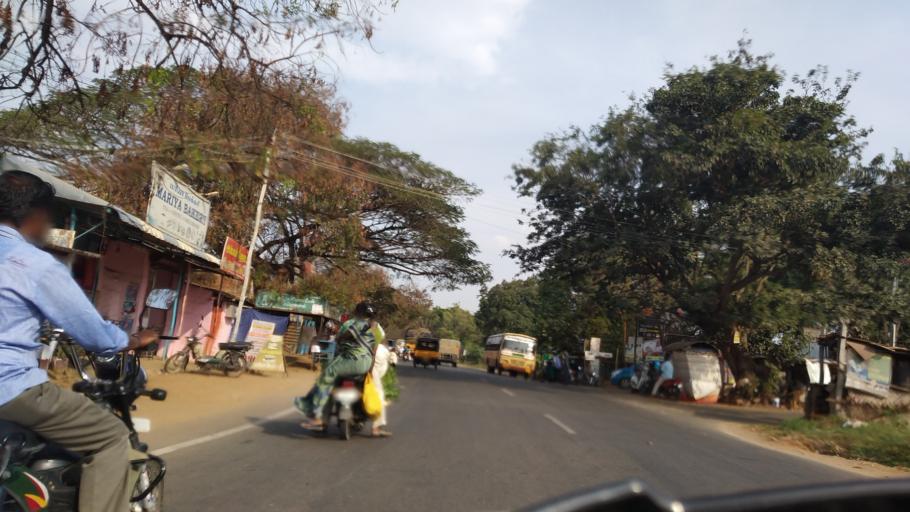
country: IN
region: Tamil Nadu
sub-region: Coimbatore
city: Perur
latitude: 10.9679
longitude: 76.9013
